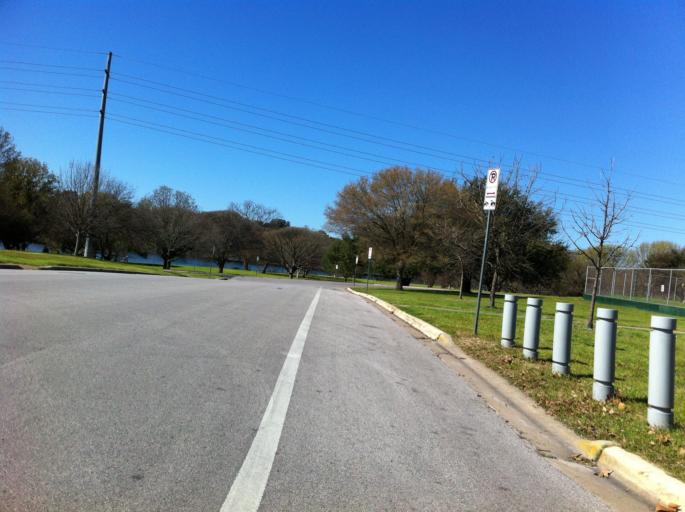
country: US
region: Texas
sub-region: Travis County
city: Austin
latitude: 30.2508
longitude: -97.7278
